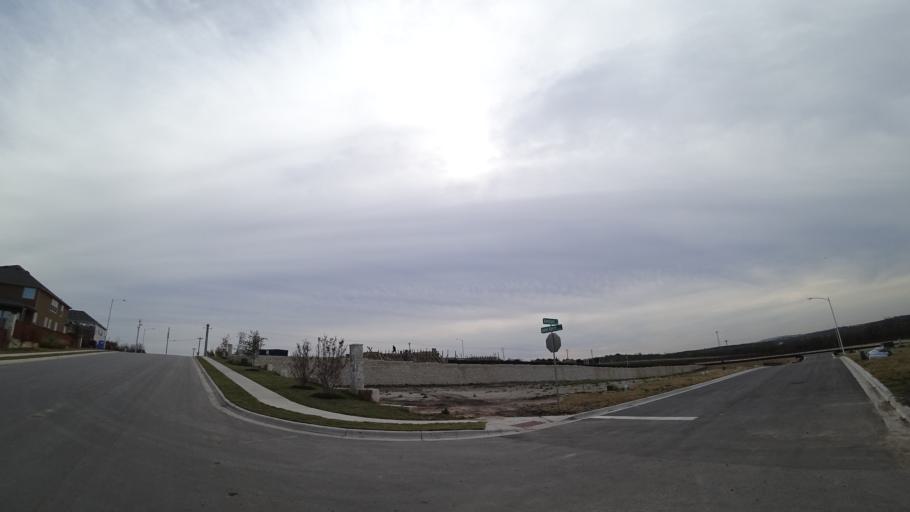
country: US
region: Texas
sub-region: Travis County
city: Onion Creek
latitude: 30.1595
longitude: -97.7301
